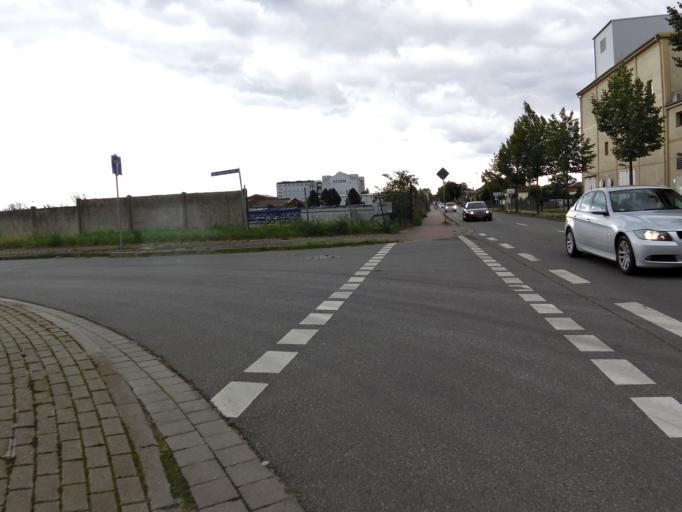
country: DE
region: Saxony-Anhalt
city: Tangermunde
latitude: 52.5589
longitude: 11.9804
